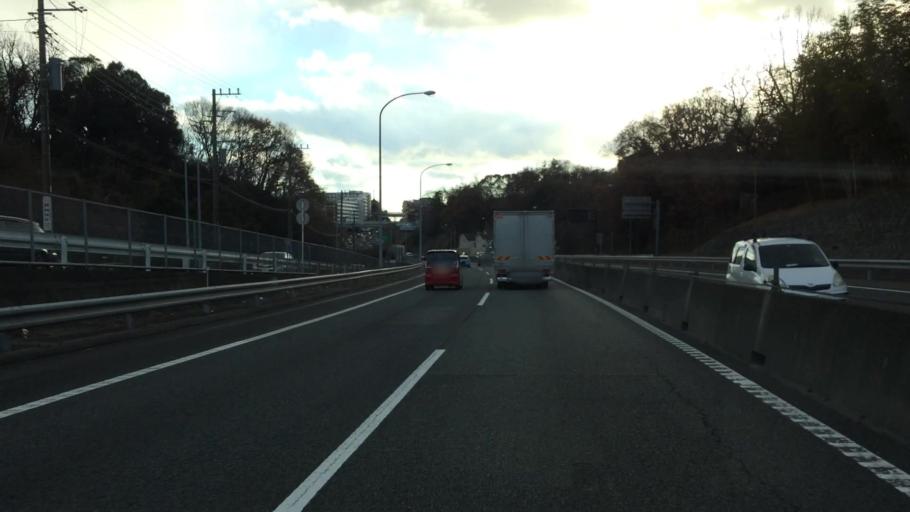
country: JP
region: Kanagawa
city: Yokohama
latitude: 35.4390
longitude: 139.5562
